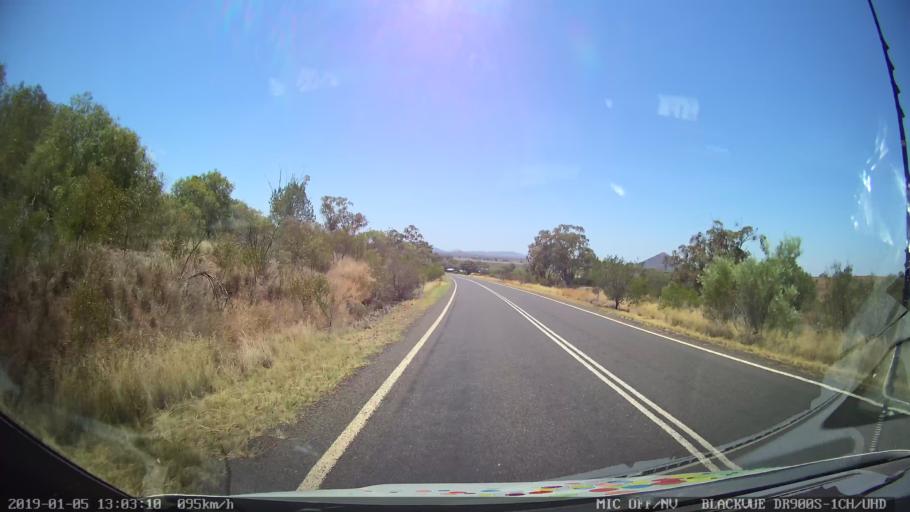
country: AU
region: New South Wales
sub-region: Gunnedah
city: Gunnedah
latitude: -31.1122
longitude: 149.8232
